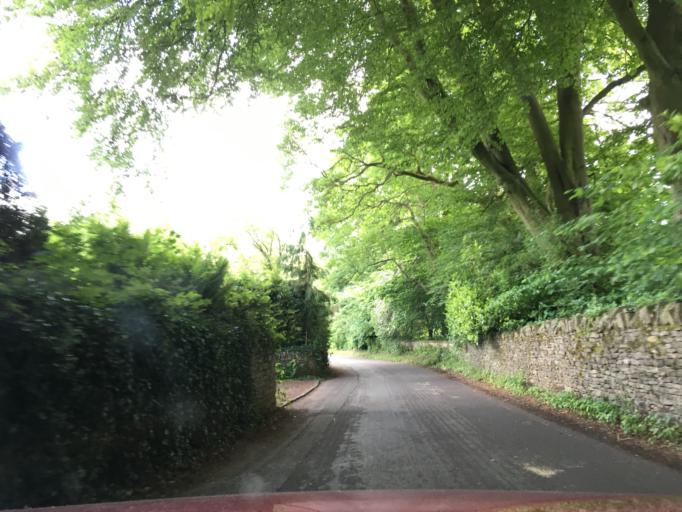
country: GB
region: England
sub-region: Gloucestershire
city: Charlton Kings
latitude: 51.8306
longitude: -2.0555
